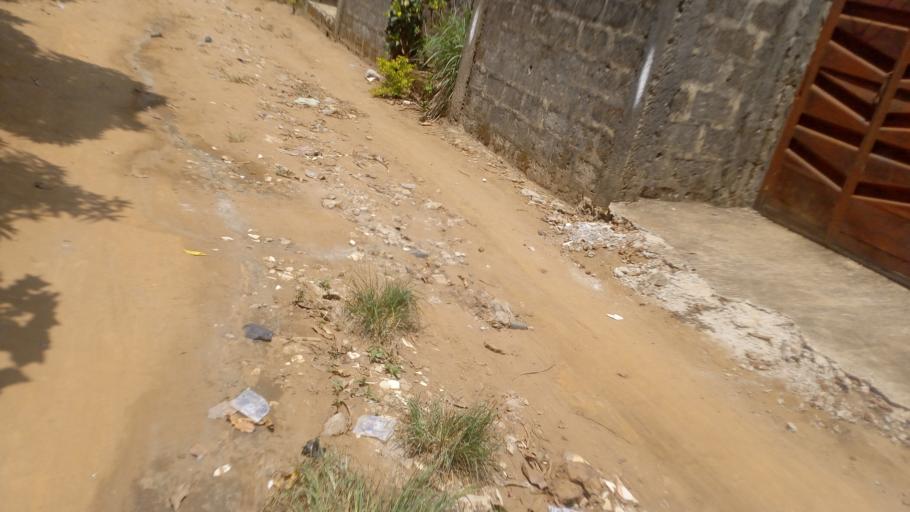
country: SL
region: Western Area
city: Waterloo
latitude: 8.3152
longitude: -13.0715
